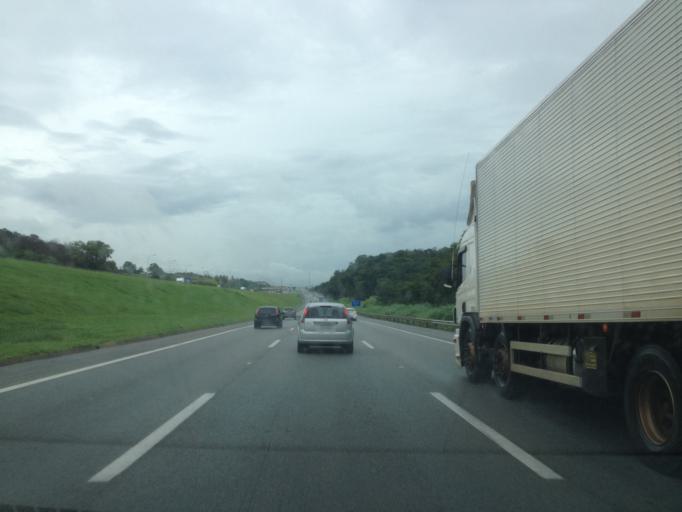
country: BR
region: Sao Paulo
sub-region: Itu
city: Itu
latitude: -23.4079
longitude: -47.2883
